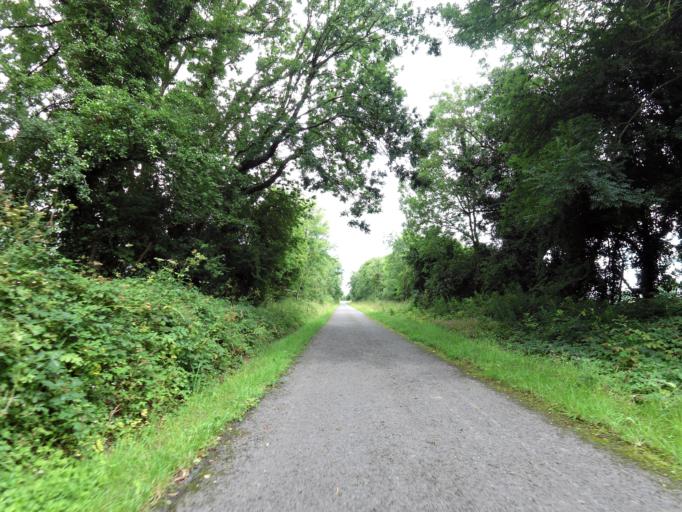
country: IE
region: Leinster
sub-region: An Iarmhi
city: An Muileann gCearr
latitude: 53.5012
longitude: -7.4342
